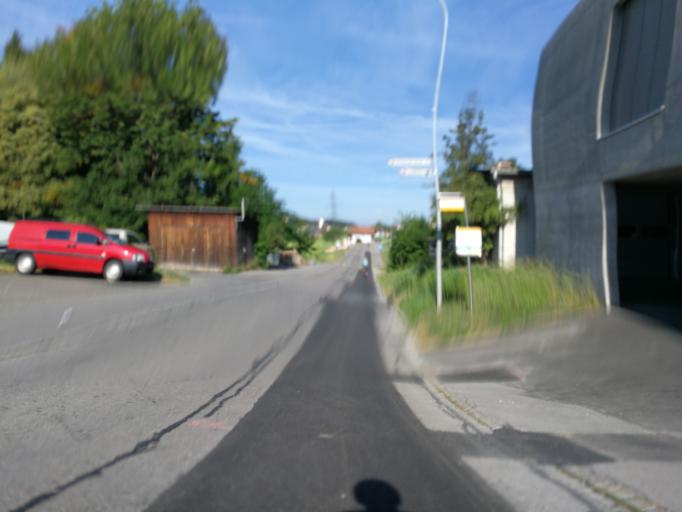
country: CH
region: Saint Gallen
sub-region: Wahlkreis See-Gaster
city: Gommiswald
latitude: 47.2370
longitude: 9.0150
